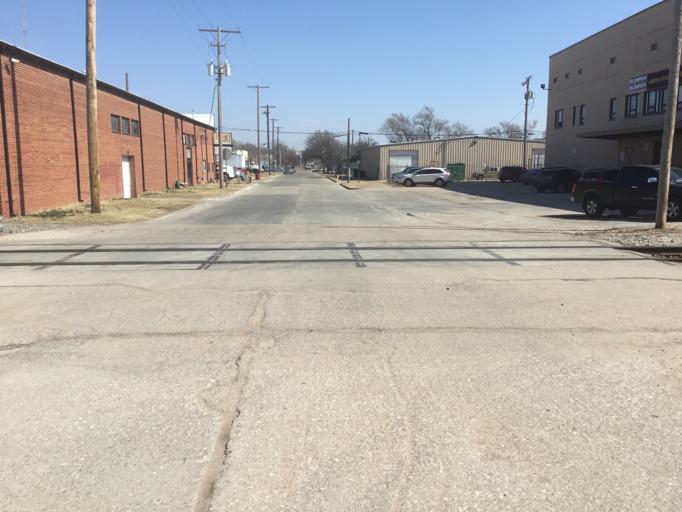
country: US
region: Kansas
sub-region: Sedgwick County
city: Wichita
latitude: 37.6680
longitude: -97.3291
